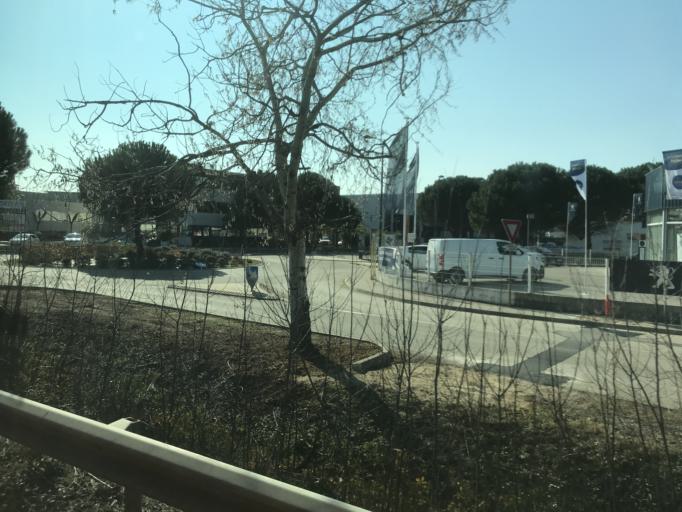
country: FR
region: Languedoc-Roussillon
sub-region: Departement de l'Herault
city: Perols
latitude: 43.5878
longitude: 3.9402
